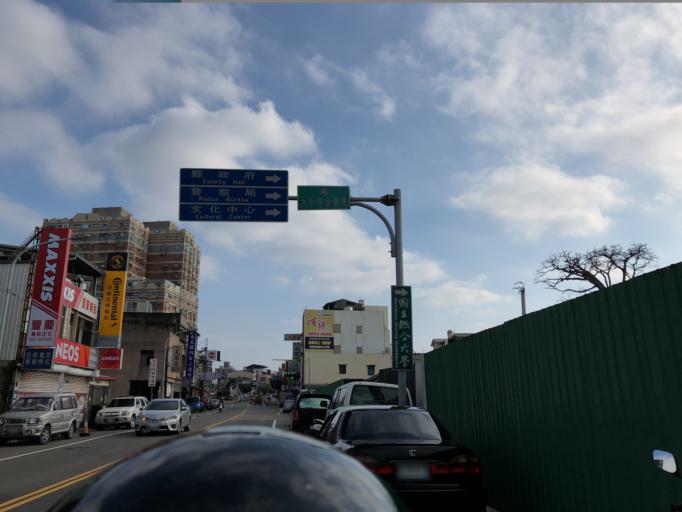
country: TW
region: Taiwan
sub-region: Miaoli
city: Miaoli
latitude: 24.5771
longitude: 120.8246
